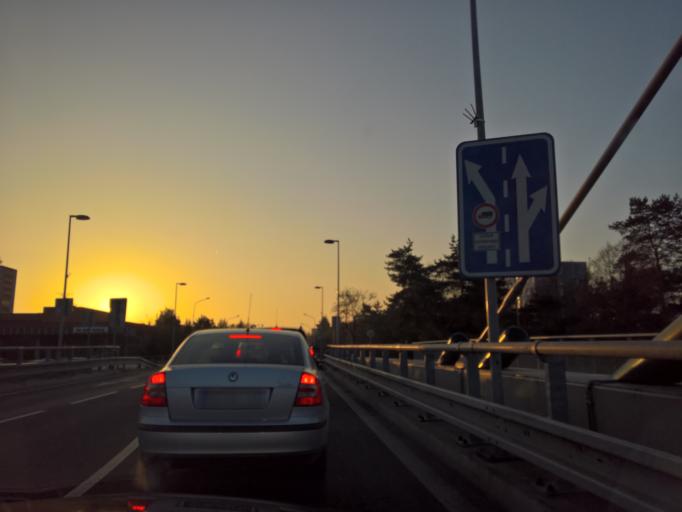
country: SK
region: Nitriansky
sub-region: Okres Nitra
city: Nitra
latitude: 48.3124
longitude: 18.0936
